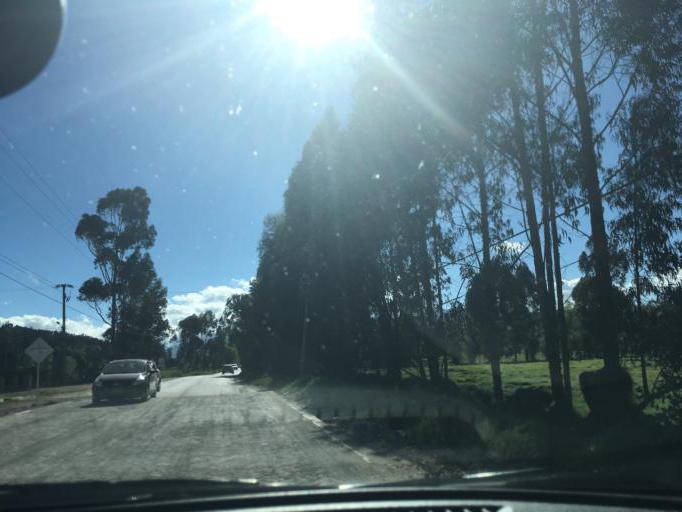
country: CO
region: Boyaca
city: Firavitoba
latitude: 5.6621
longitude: -72.9737
